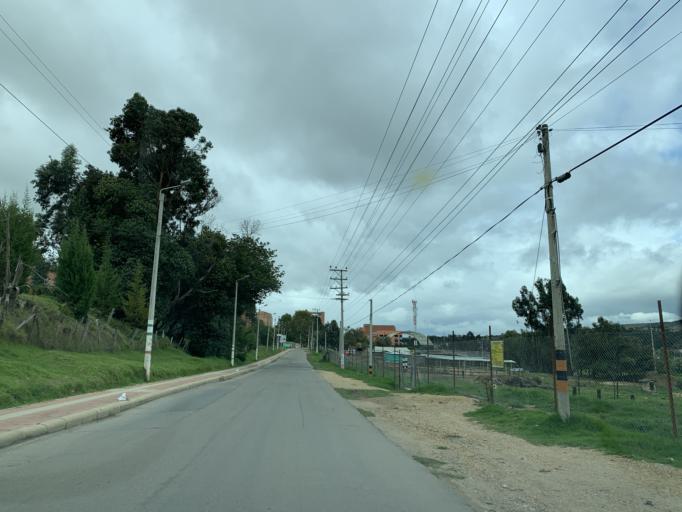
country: CO
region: Boyaca
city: Tunja
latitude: 5.5644
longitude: -73.3423
